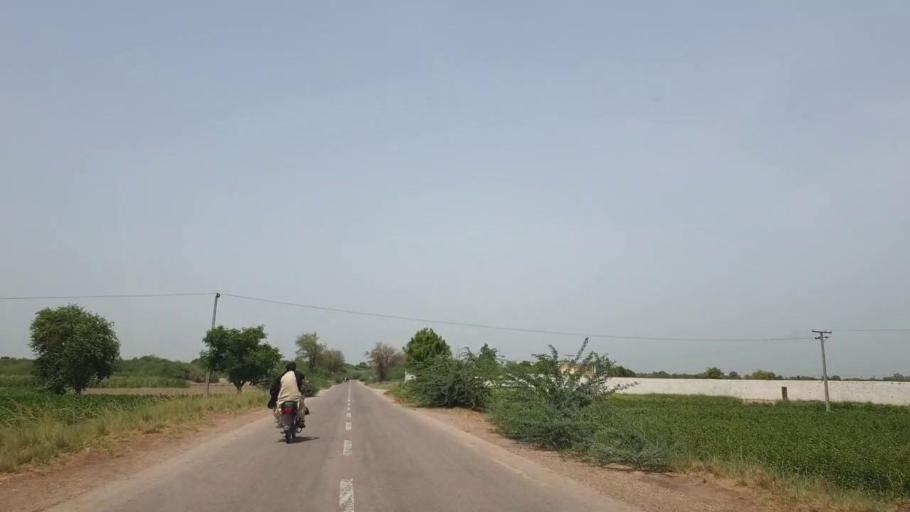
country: PK
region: Sindh
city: Sakrand
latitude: 26.1936
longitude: 68.2370
